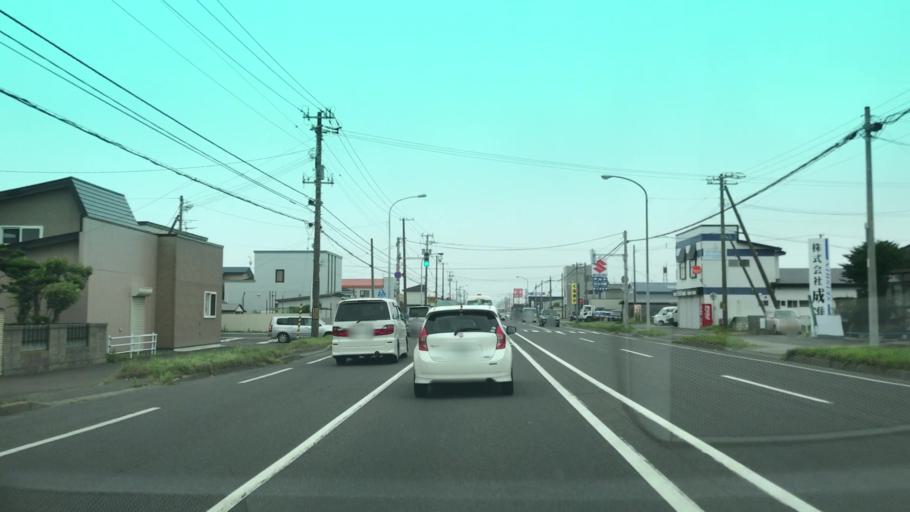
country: JP
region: Hokkaido
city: Muroran
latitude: 42.3764
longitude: 141.0691
